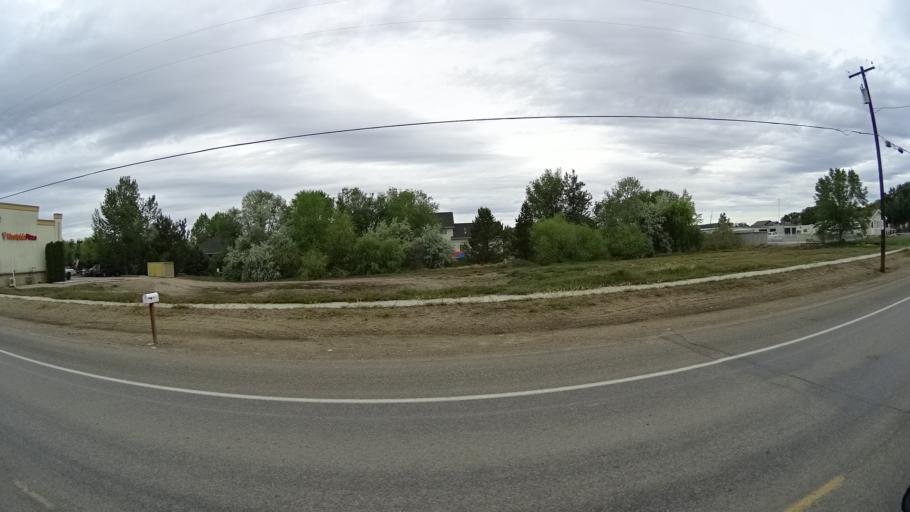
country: US
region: Idaho
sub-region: Ada County
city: Star
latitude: 43.6864
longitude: -116.4931
